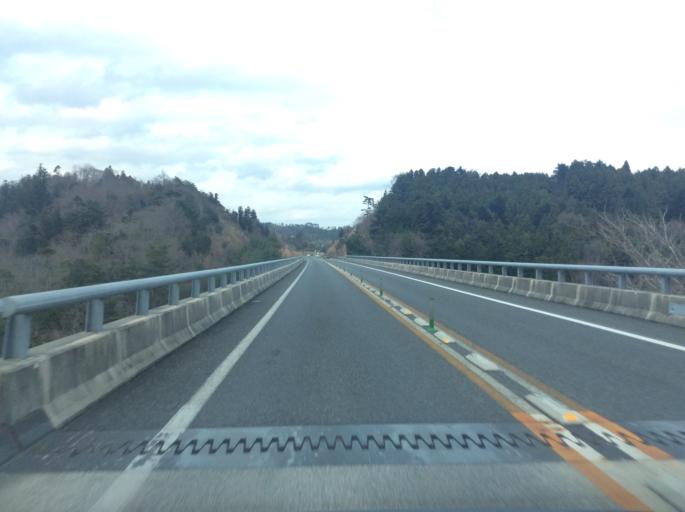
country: JP
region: Fukushima
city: Iwaki
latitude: 37.1591
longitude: 140.9665
